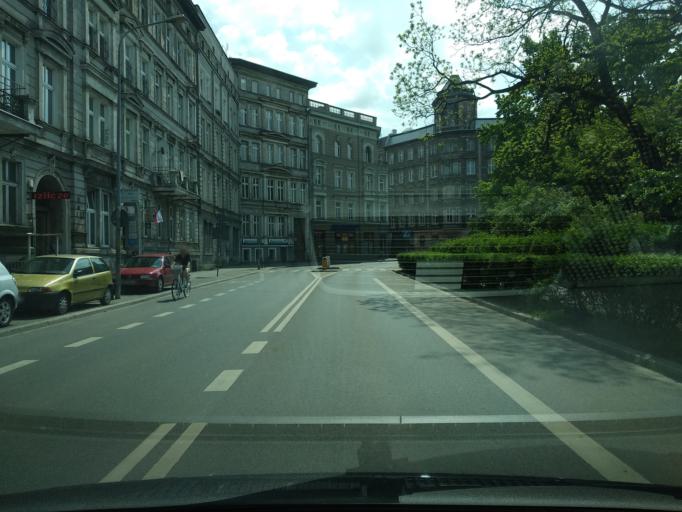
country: PL
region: Lower Silesian Voivodeship
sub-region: Powiat wroclawski
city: Wroclaw
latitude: 51.1199
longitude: 17.0367
